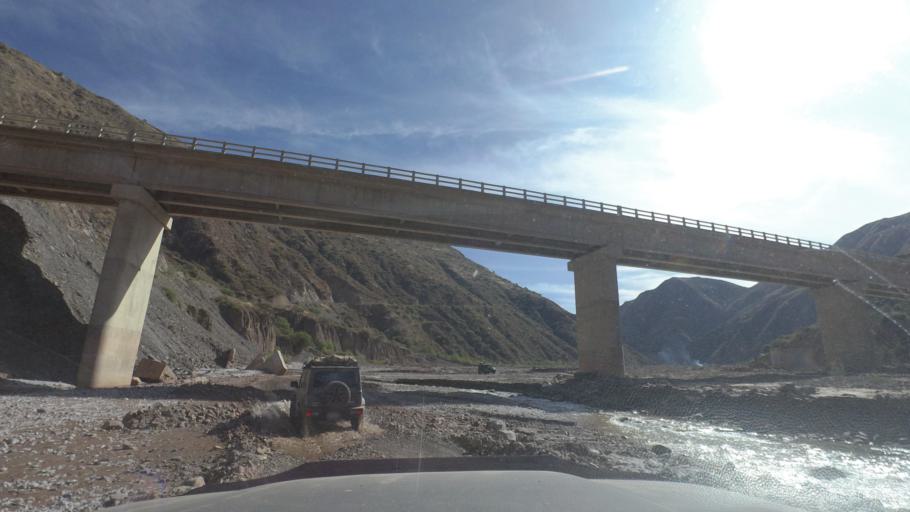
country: BO
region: Cochabamba
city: Irpa Irpa
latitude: -17.8550
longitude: -66.4309
